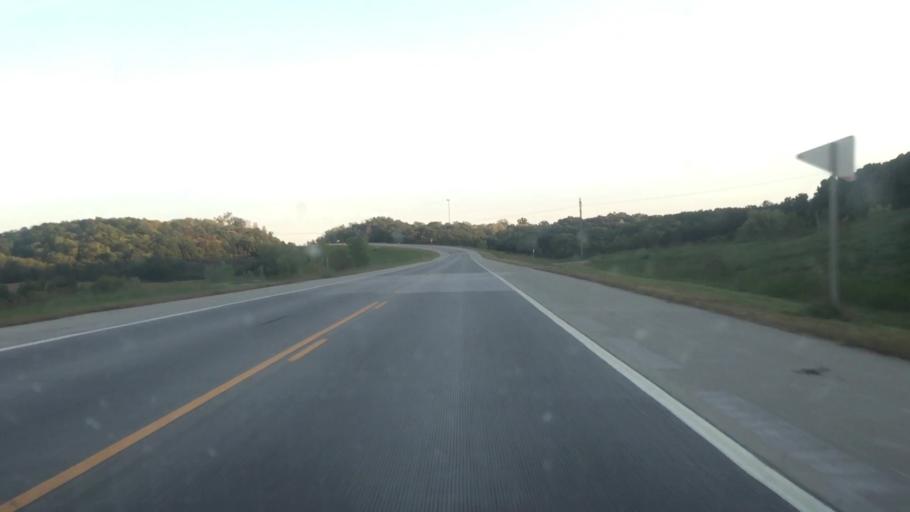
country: US
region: Kansas
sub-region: Leavenworth County
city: Leavenworth
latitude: 39.3435
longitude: -94.9620
